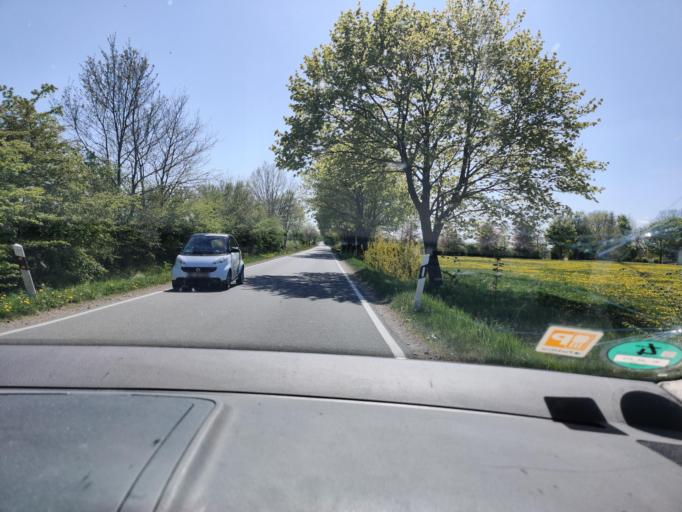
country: DE
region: Schleswig-Holstein
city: Sankelmark
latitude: 54.7014
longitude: 9.3939
